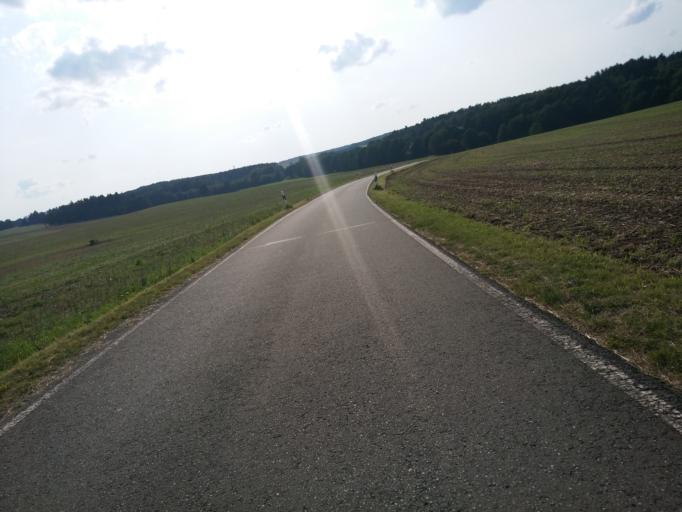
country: DE
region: Saxony
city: Syrau
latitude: 50.5620
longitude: 12.1225
